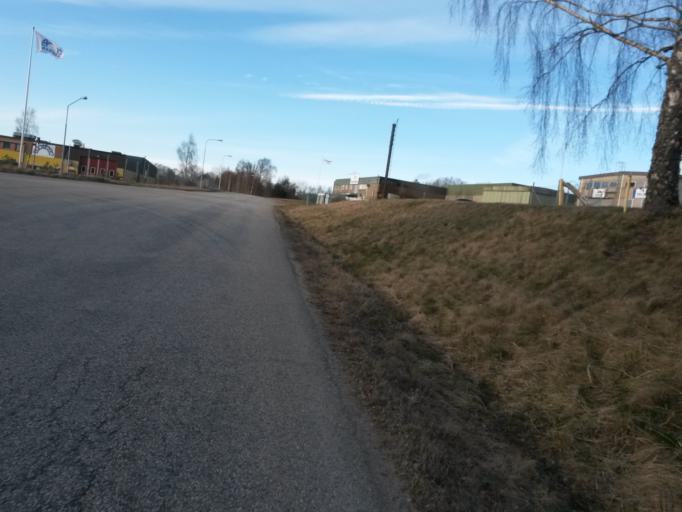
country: SE
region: Vaestra Goetaland
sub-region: Vargarda Kommun
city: Vargarda
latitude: 58.0279
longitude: 12.7912
